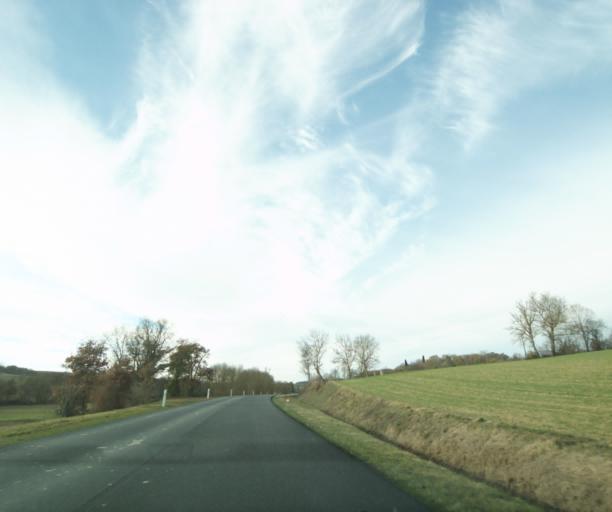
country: FR
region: Midi-Pyrenees
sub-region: Departement du Gers
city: Jegun
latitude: 43.6821
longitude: 0.4956
